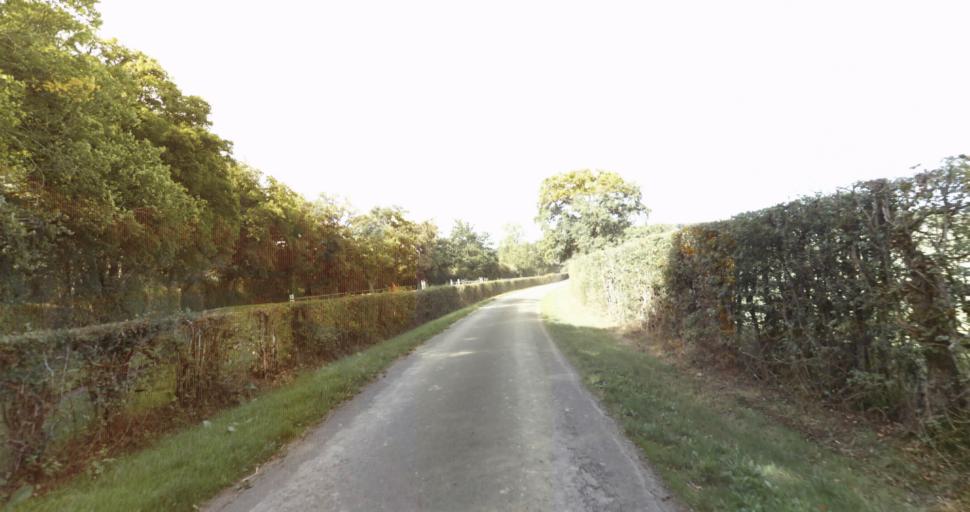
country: FR
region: Lower Normandy
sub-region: Departement de l'Orne
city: Sees
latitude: 48.7035
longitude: 0.1765
